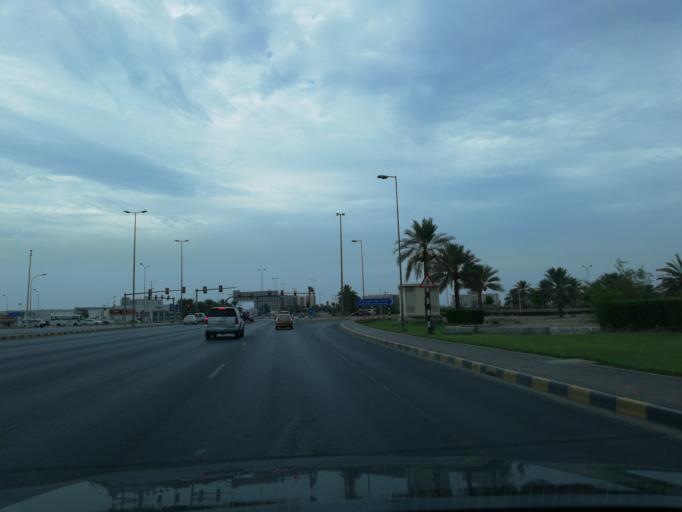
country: OM
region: Muhafazat Masqat
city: Bawshar
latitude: 23.5811
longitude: 58.3816
